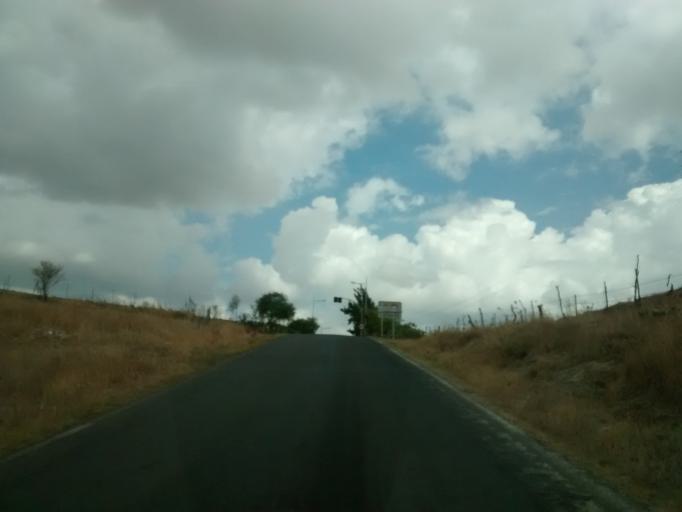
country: ES
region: Andalusia
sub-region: Provincia de Cadiz
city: Paterna de Rivera
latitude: 36.5190
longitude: -5.8684
